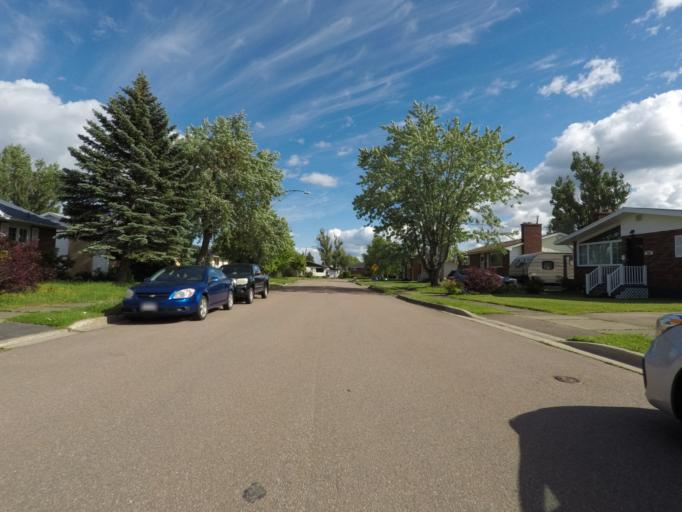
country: CA
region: New Brunswick
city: Moncton
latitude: 46.0979
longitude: -64.8264
